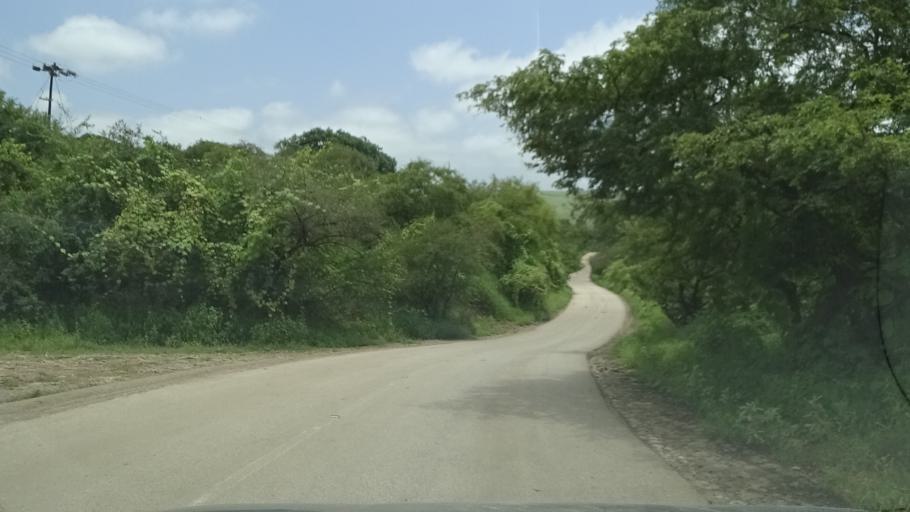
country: OM
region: Zufar
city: Salalah
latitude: 17.1960
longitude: 54.1760
